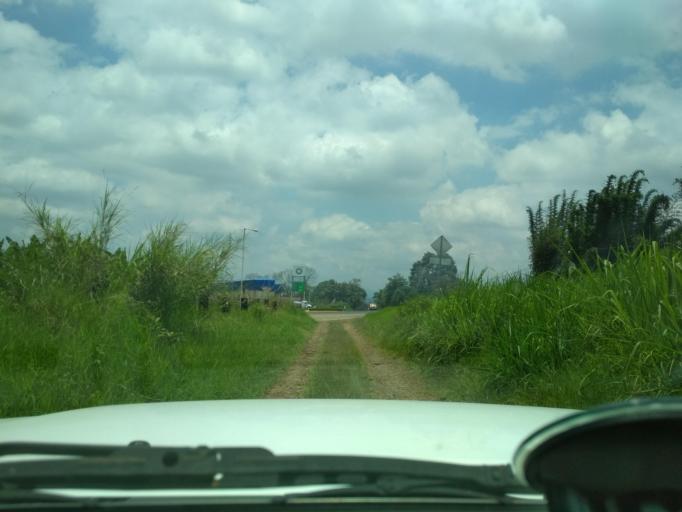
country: MX
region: Veracruz
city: Tocuila
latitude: 18.9495
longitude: -97.0174
